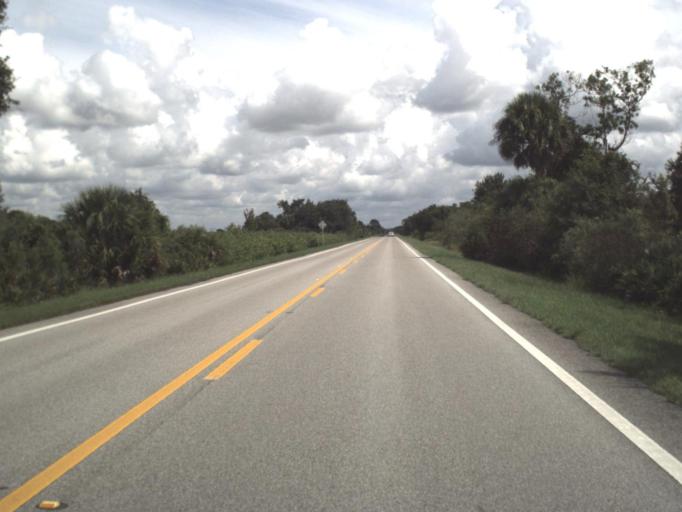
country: US
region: Florida
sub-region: Sarasota County
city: Warm Mineral Springs
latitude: 27.2148
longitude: -82.2664
